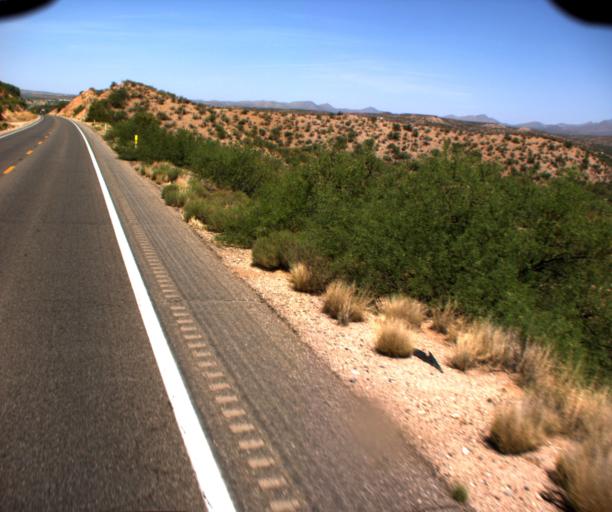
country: US
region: Arizona
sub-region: Gila County
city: Globe
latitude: 33.3487
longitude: -110.6318
